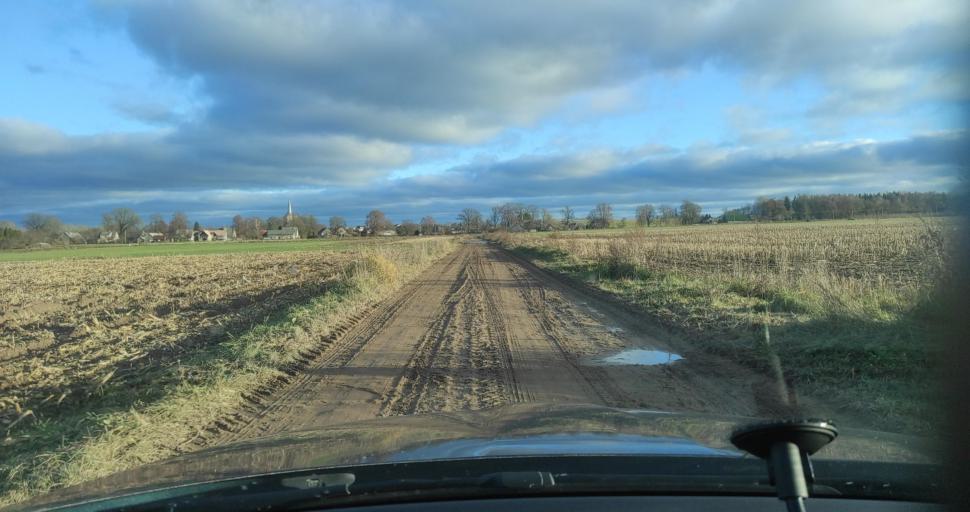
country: LV
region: Kuldigas Rajons
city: Kuldiga
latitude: 57.2696
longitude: 22.0251
